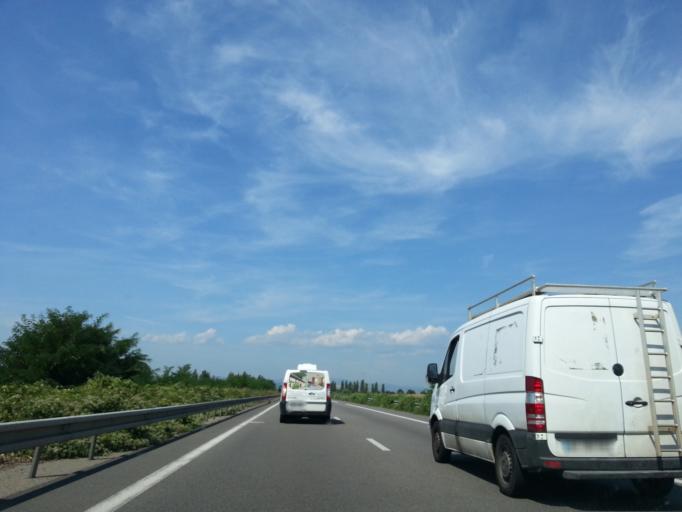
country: FR
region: Alsace
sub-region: Departement du Bas-Rhin
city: Entzheim
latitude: 48.5225
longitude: 7.6288
